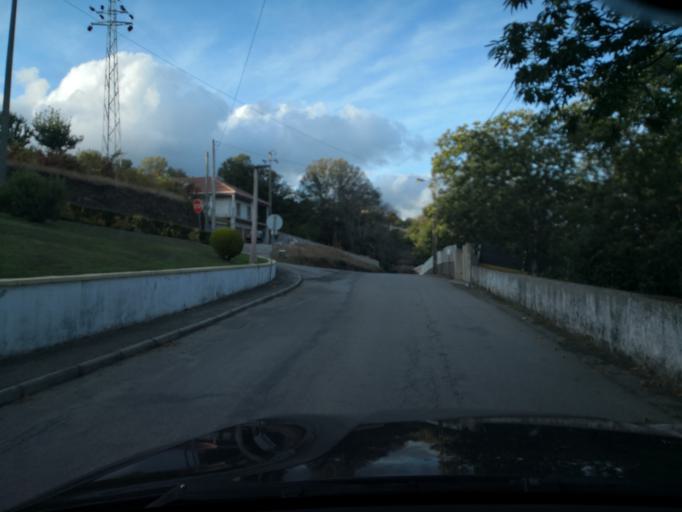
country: PT
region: Vila Real
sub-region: Santa Marta de Penaguiao
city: Santa Marta de Penaguiao
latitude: 41.2255
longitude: -7.8189
